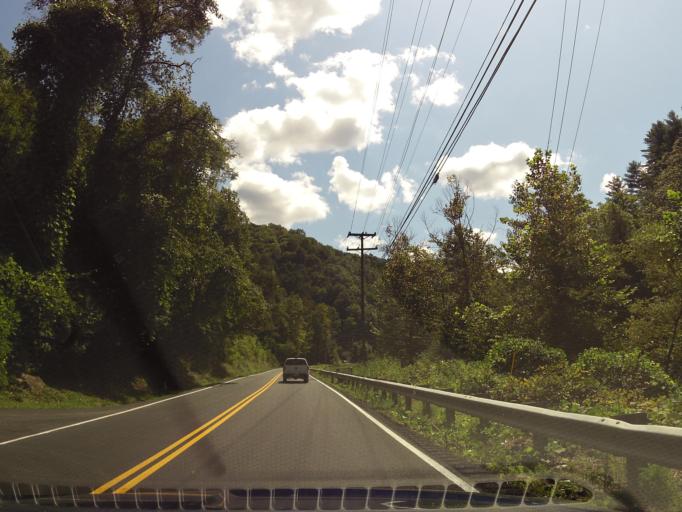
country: US
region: Kentucky
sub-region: Leslie County
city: Hyden
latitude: 37.0082
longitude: -83.3990
